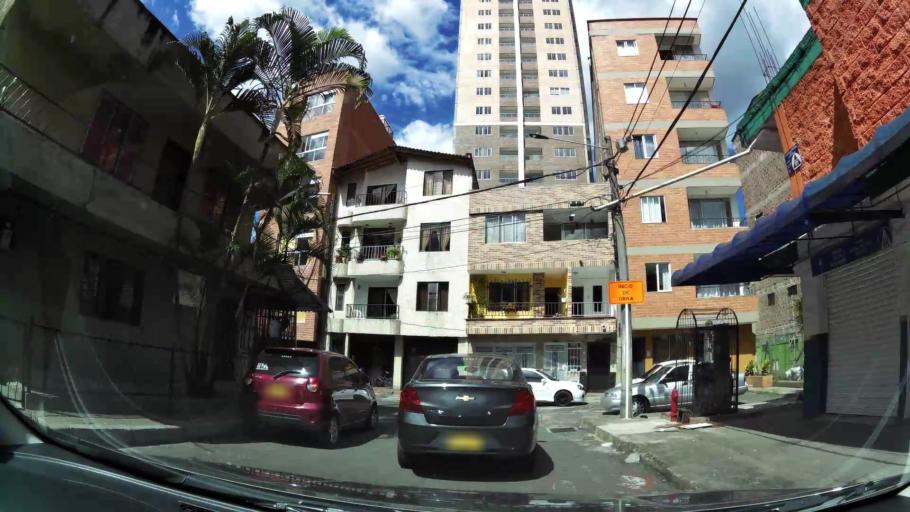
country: CO
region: Antioquia
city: Sabaneta
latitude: 6.1517
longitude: -75.6215
